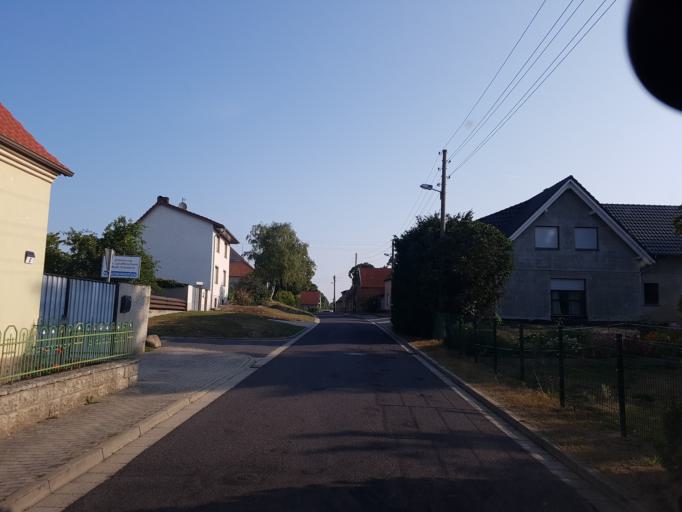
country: DE
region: Brandenburg
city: Finsterwalde
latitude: 51.6640
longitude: 13.7373
